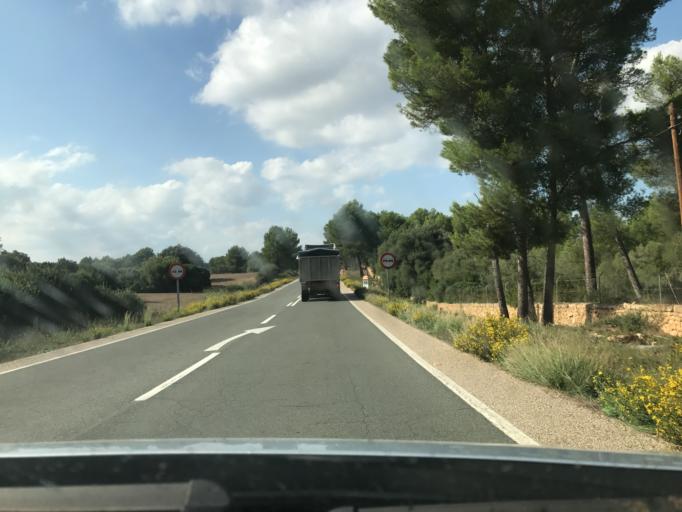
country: ES
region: Balearic Islands
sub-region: Illes Balears
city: Santa Margalida
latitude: 39.7256
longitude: 3.2053
